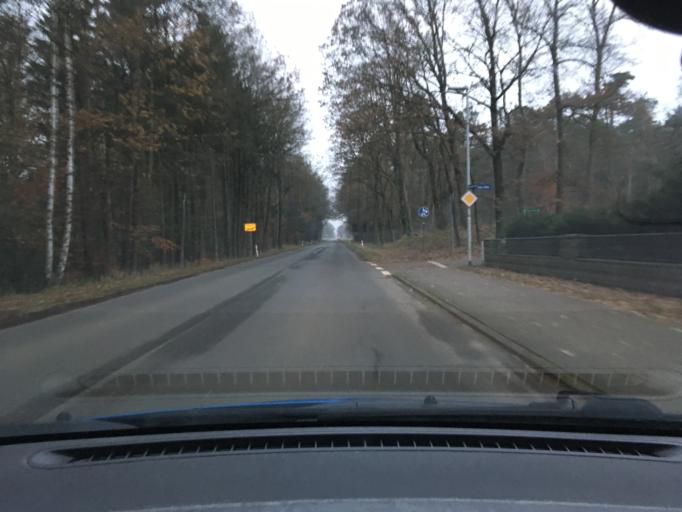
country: DE
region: Lower Saxony
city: Bispingen
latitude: 53.1174
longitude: 9.9541
